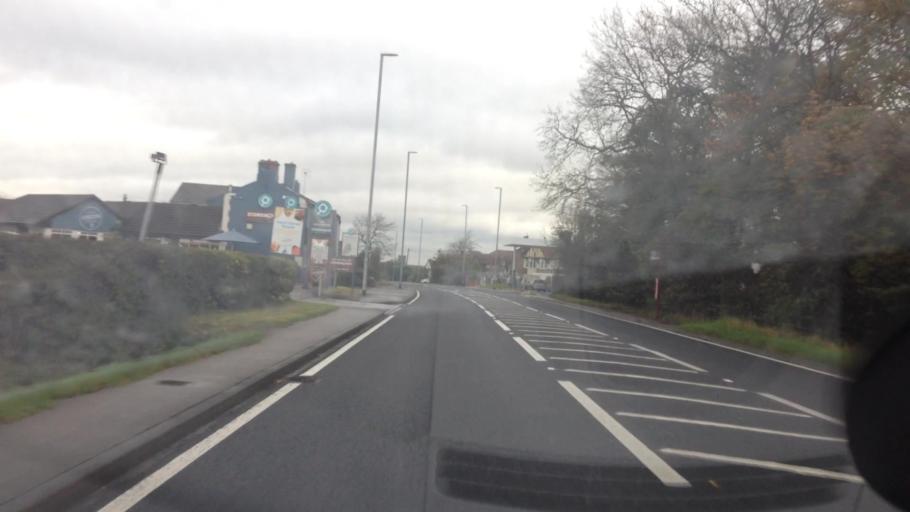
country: GB
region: England
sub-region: City and Borough of Leeds
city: Shadwell
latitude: 53.8432
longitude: -1.4676
